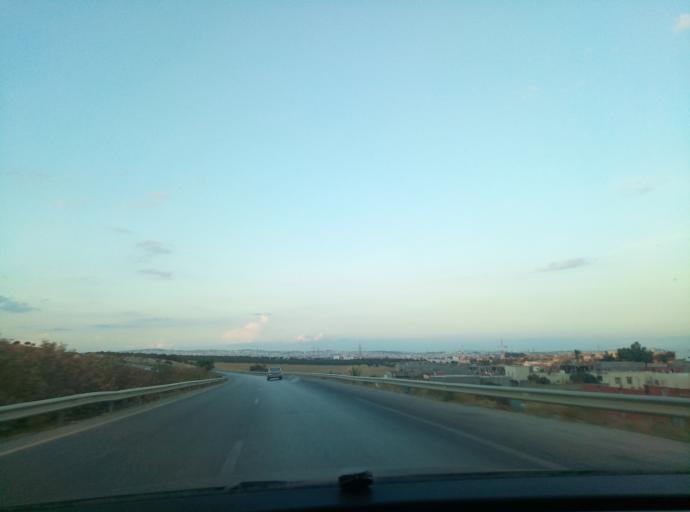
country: TN
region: Manouba
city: Manouba
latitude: 36.7658
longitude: 10.0688
